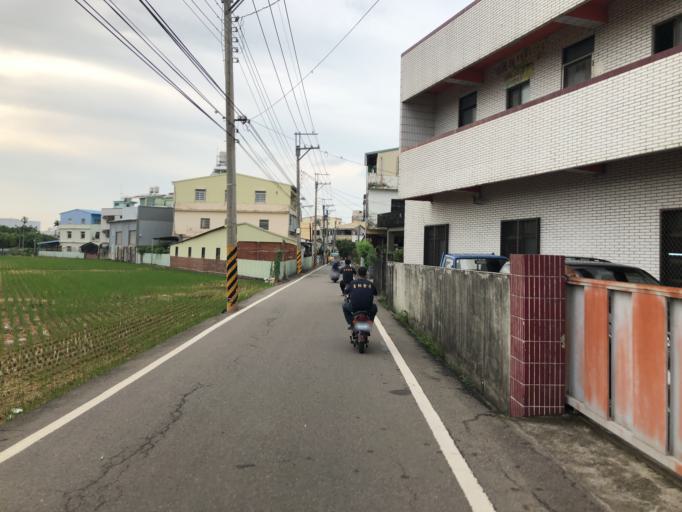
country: TW
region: Taiwan
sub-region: Taichung City
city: Taichung
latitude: 24.0602
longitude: 120.6829
